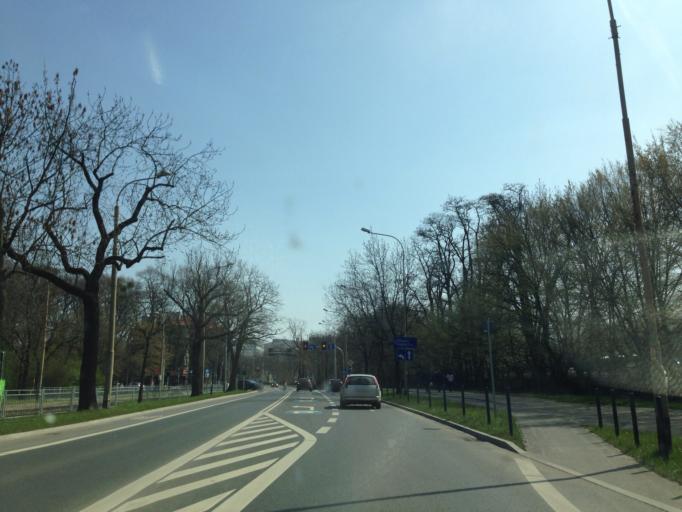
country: PL
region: Lower Silesian Voivodeship
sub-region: Powiat wroclawski
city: Wroclaw
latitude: 51.1056
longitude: 17.0774
